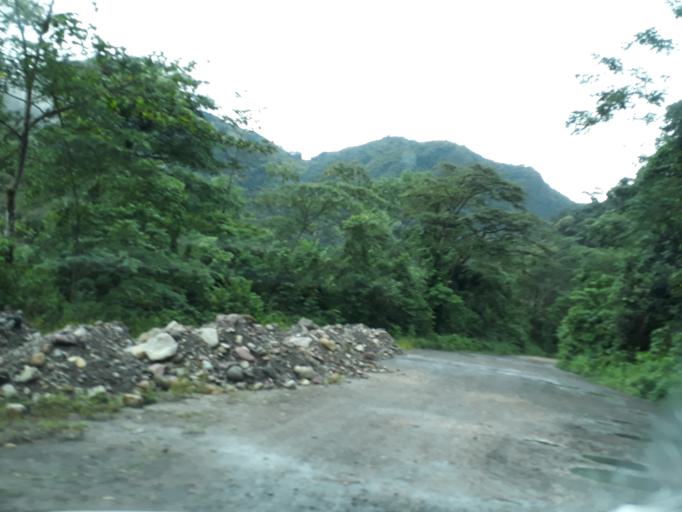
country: CO
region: Boyaca
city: Santa Maria
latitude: 4.7522
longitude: -73.3109
